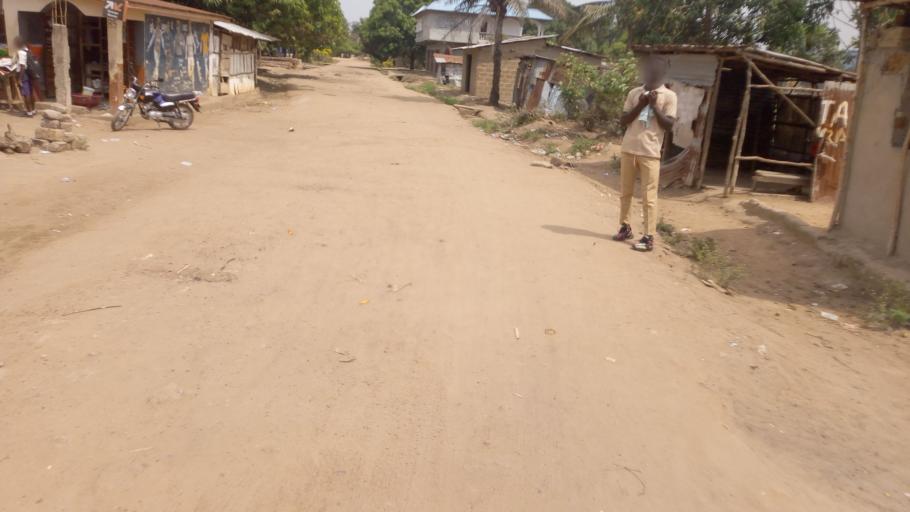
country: SL
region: Western Area
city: Waterloo
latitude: 8.3101
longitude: -13.0658
